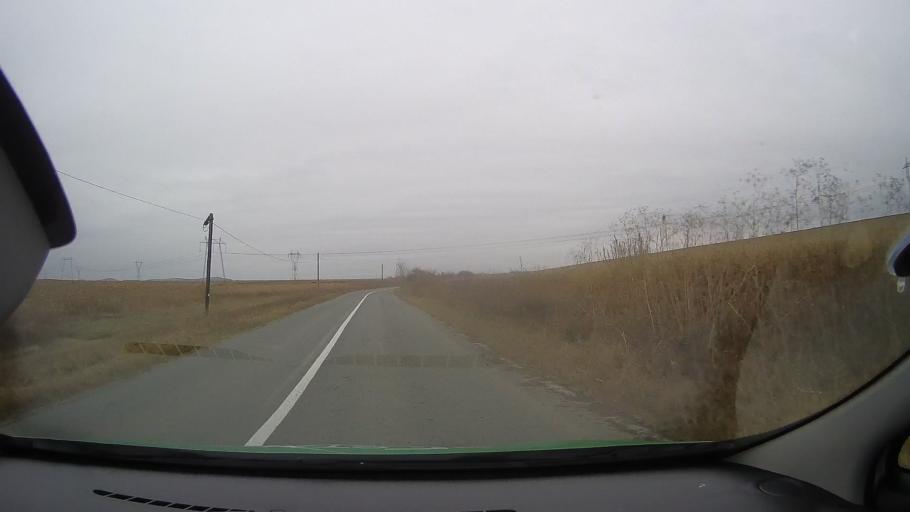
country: RO
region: Constanta
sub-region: Comuna Silistea
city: Silistea
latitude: 44.4338
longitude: 28.2198
